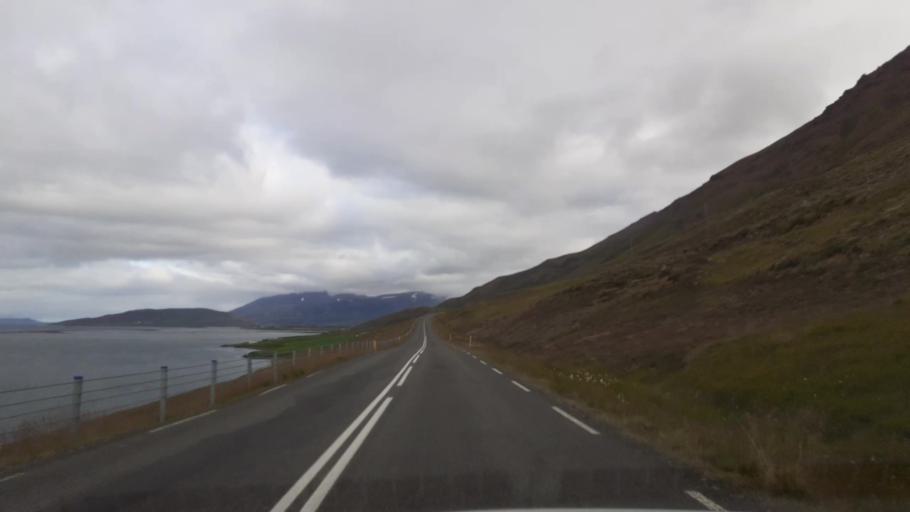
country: IS
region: Northeast
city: Akureyri
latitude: 65.8434
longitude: -18.0574
